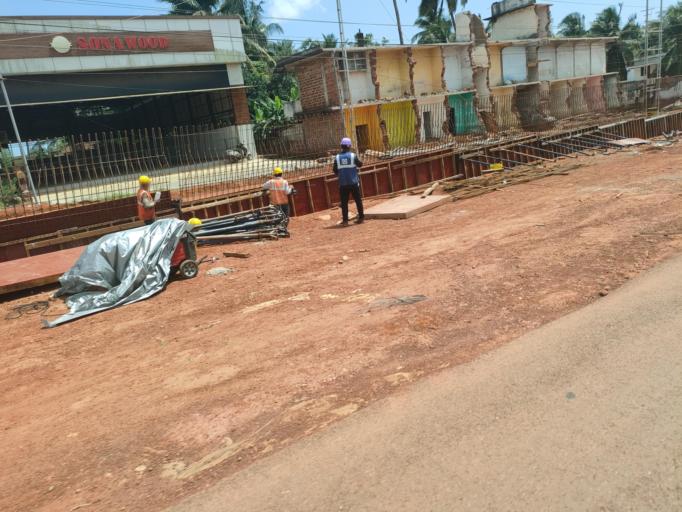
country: IN
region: Kerala
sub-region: Kasaragod District
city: Kasaragod
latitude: 12.5114
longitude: 75.0326
